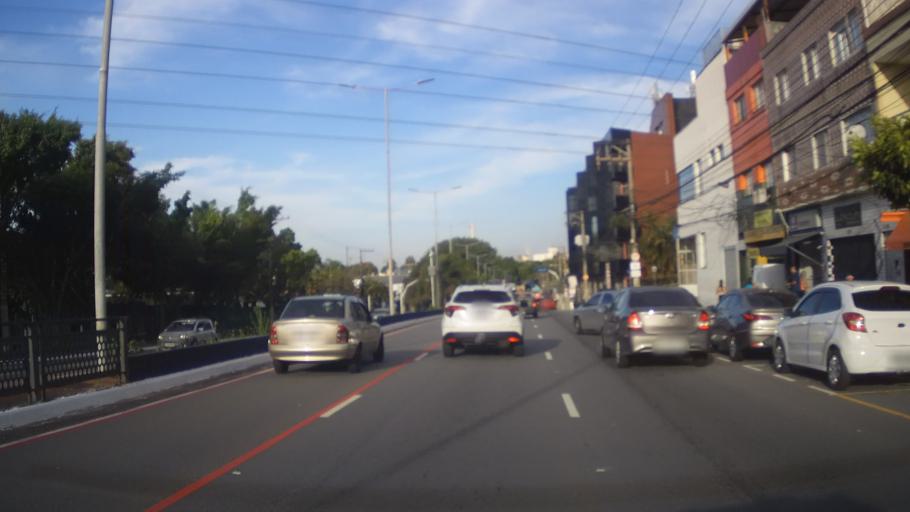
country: BR
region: Sao Paulo
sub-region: Sao Caetano Do Sul
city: Sao Caetano do Sul
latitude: -23.6166
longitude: -46.5594
